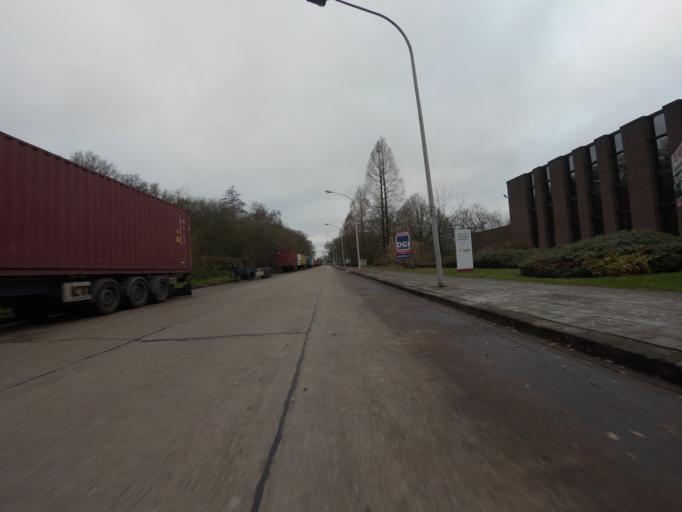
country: BE
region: Flanders
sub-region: Provincie Antwerpen
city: Aartselaar
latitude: 51.1550
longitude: 4.3686
